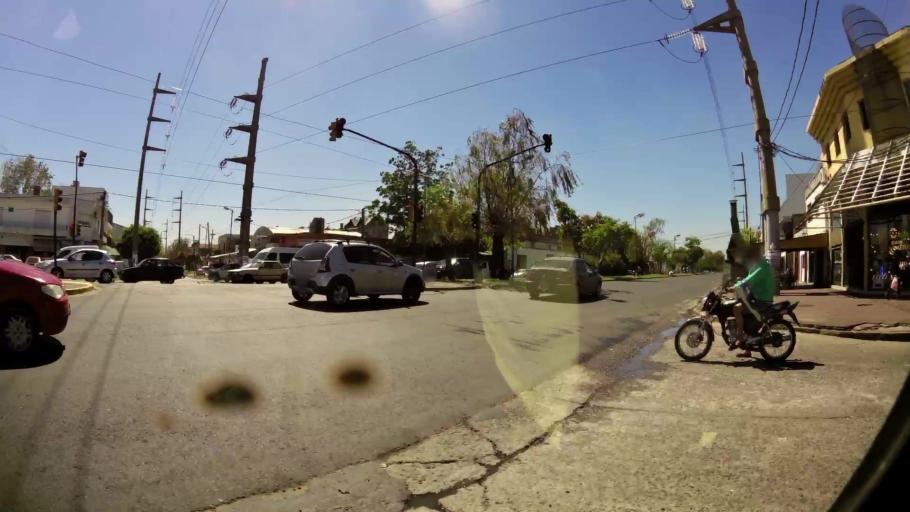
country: AR
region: Buenos Aires
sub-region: Partido de Quilmes
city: Quilmes
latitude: -34.7138
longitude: -58.3019
